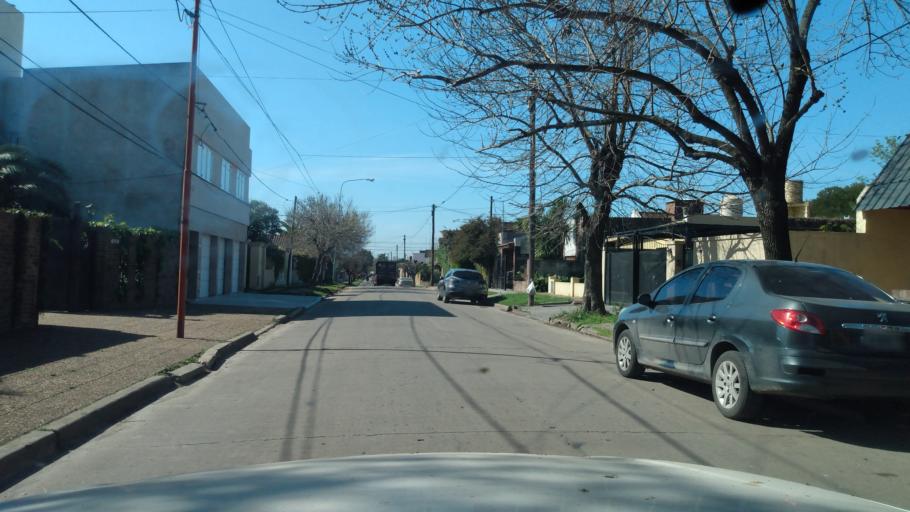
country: AR
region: Buenos Aires
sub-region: Partido de Lujan
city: Lujan
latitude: -34.5747
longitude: -59.1020
